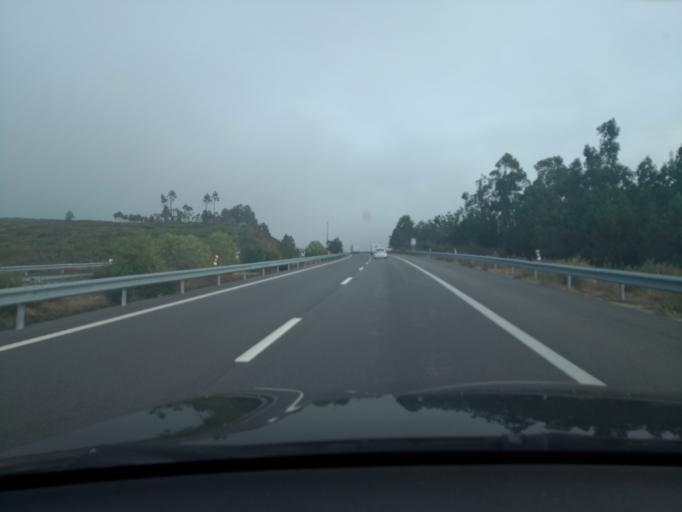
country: PT
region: Braga
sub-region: Fafe
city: Fafe
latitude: 41.4439
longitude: -8.0892
